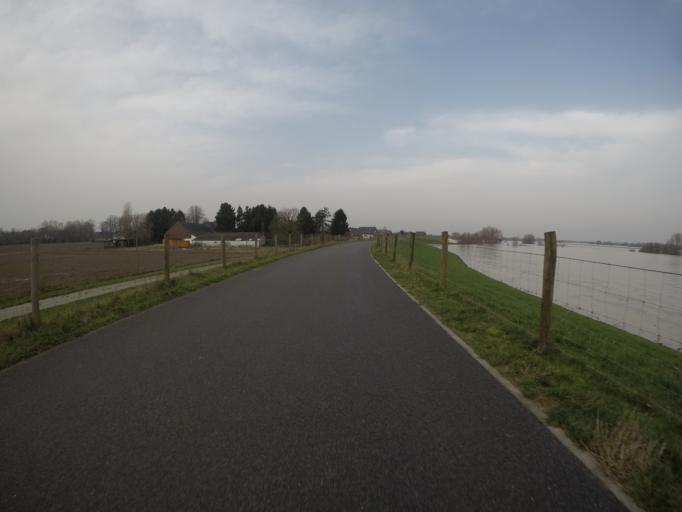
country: DE
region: North Rhine-Westphalia
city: Rees
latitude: 51.7085
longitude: 6.4162
